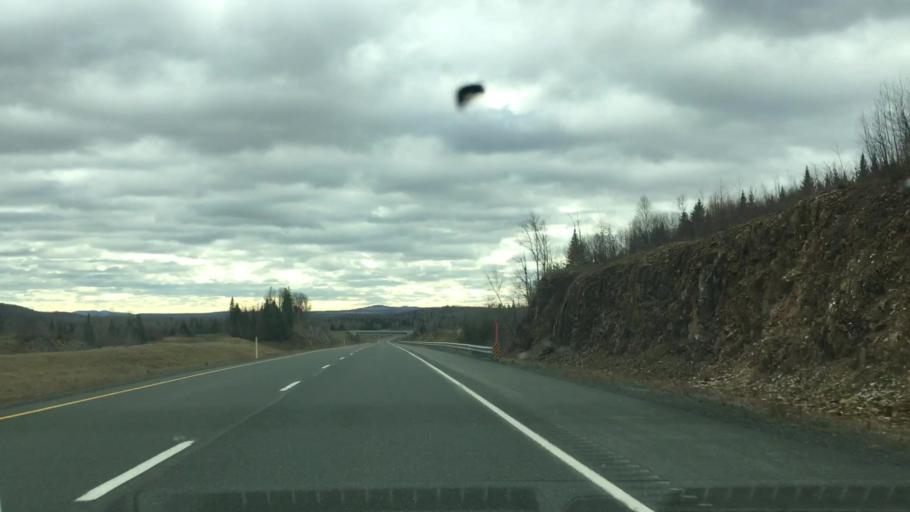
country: US
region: Maine
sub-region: Aroostook County
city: Easton
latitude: 46.6317
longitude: -67.7422
